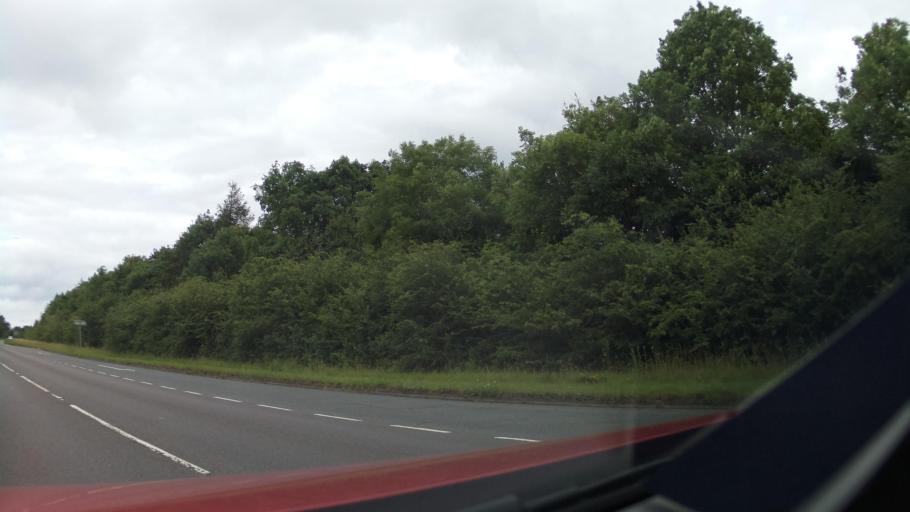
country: GB
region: England
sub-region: Northamptonshire
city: Geddington
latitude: 52.4665
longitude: -0.7398
